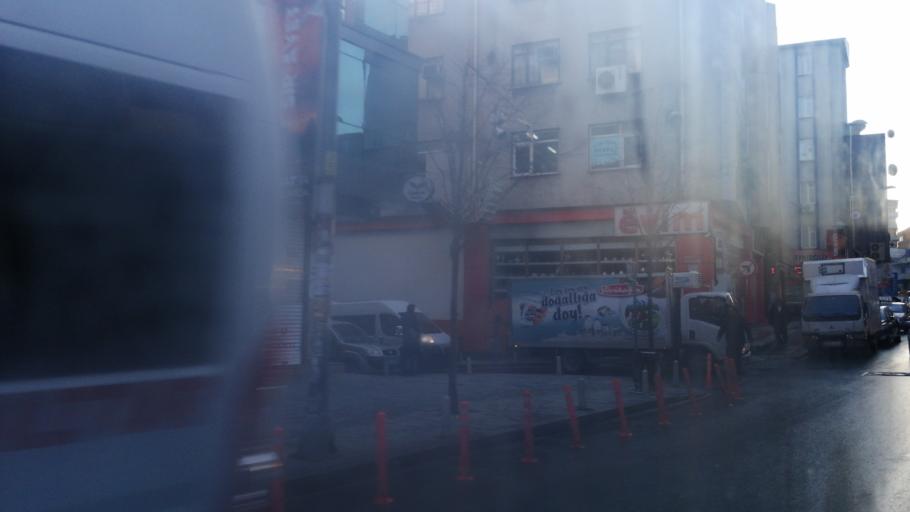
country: TR
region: Istanbul
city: Sisli
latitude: 41.0793
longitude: 28.9956
